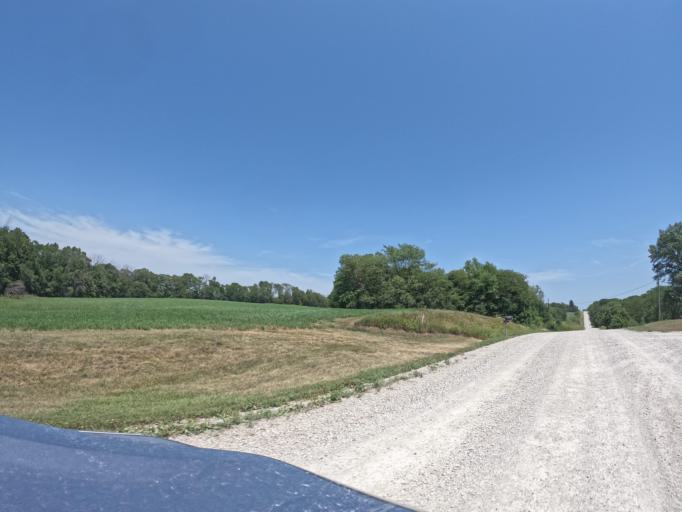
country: US
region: Iowa
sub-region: Henry County
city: Mount Pleasant
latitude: 40.9450
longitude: -91.6732
